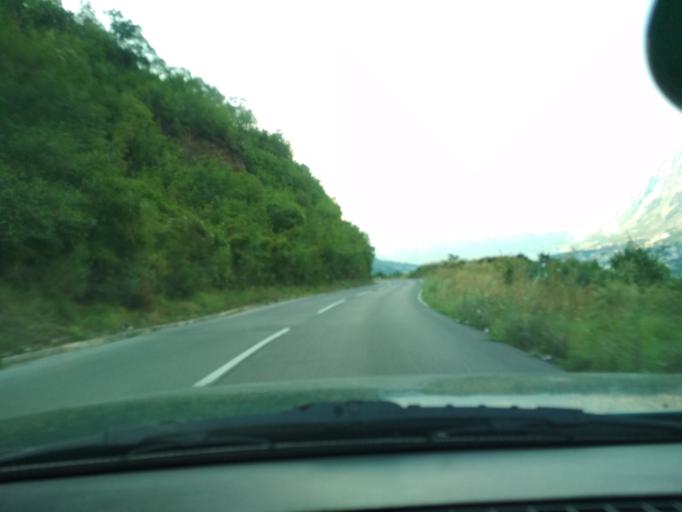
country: ME
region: Kotor
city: Kotor
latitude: 42.4097
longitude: 18.7649
